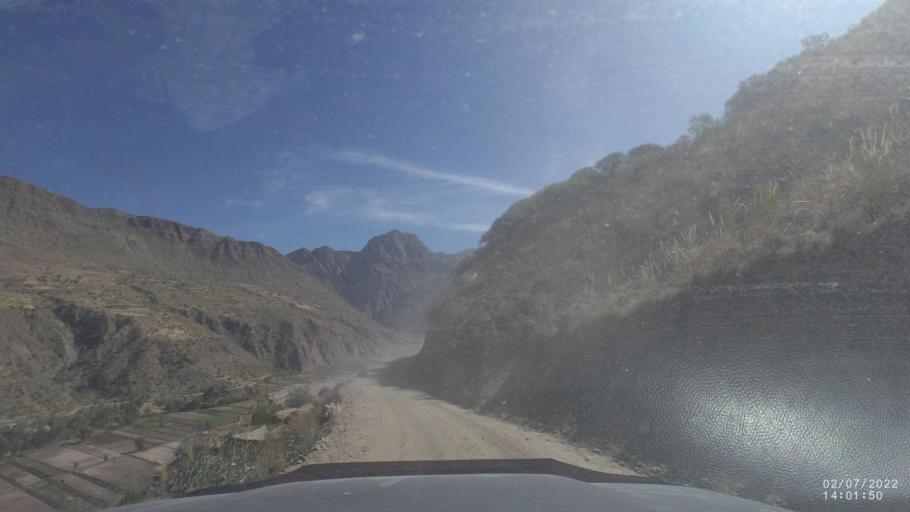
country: BO
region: Cochabamba
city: Irpa Irpa
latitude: -17.8251
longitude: -66.3846
